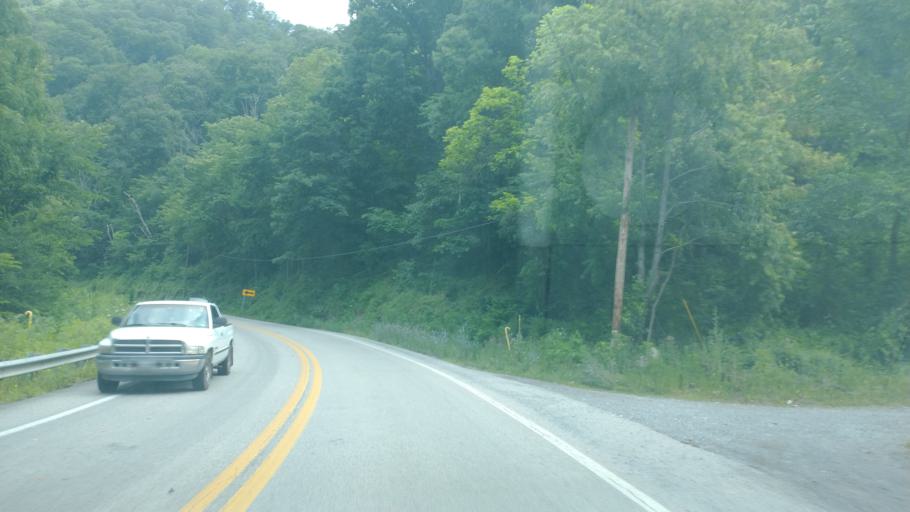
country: US
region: West Virginia
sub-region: McDowell County
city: Welch
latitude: 37.4201
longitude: -81.4813
